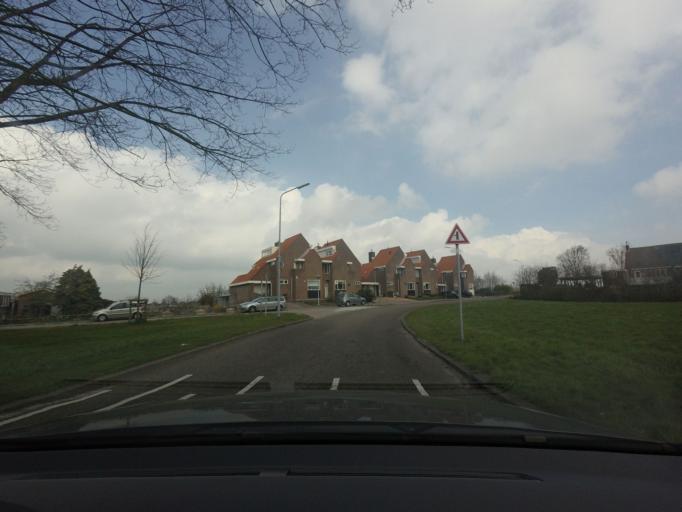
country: NL
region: North Holland
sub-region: Gemeente Haarlemmermeer
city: Hoofddorp
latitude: 52.3531
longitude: 4.7591
